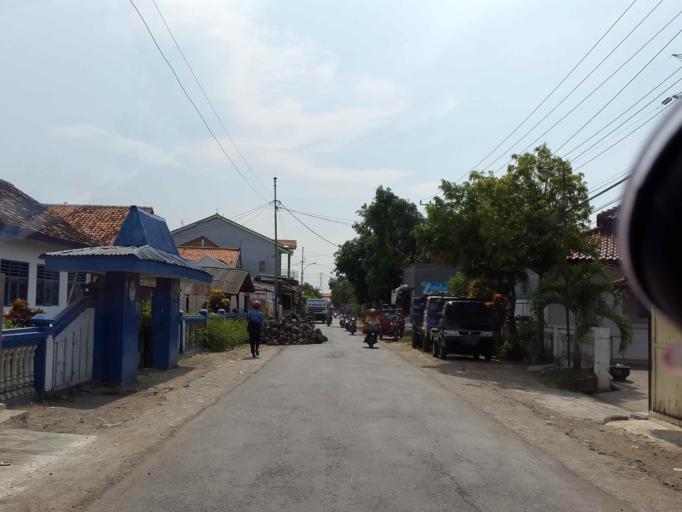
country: ID
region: Central Java
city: Pemalang
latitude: -6.9149
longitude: 109.3849
